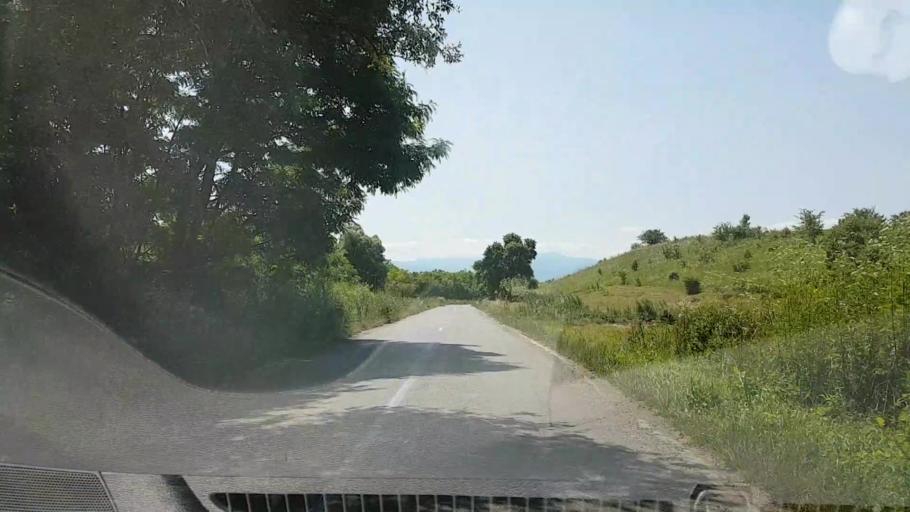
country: RO
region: Brasov
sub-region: Comuna Cincu
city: Cincu
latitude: 45.8869
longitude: 24.8131
